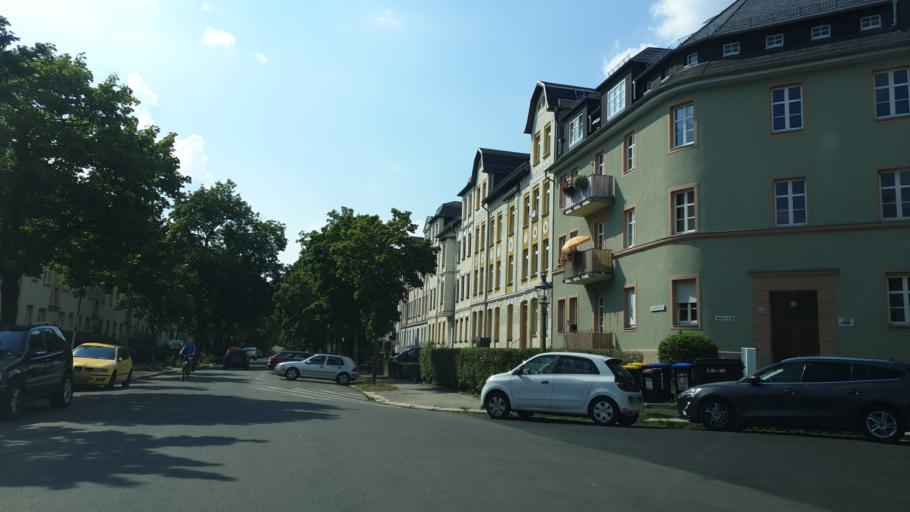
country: DE
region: Saxony
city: Chemnitz
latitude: 50.8331
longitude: 12.9523
